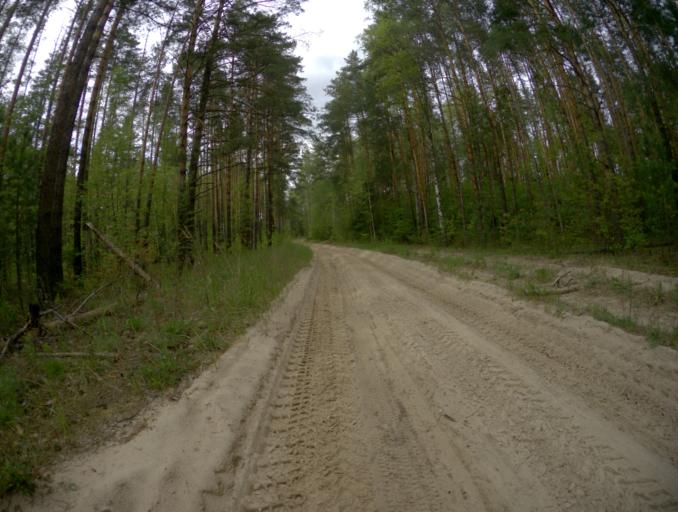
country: RU
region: Rjazan
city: Gus'-Zheleznyy
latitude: 55.0230
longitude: 41.1811
